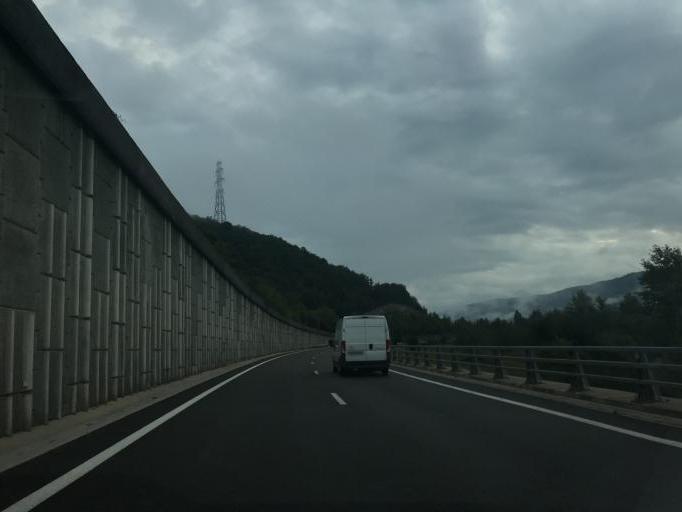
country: FR
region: Rhone-Alpes
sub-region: Departement de l'Ain
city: Montreal-la-Cluse
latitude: 46.1926
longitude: 5.5776
